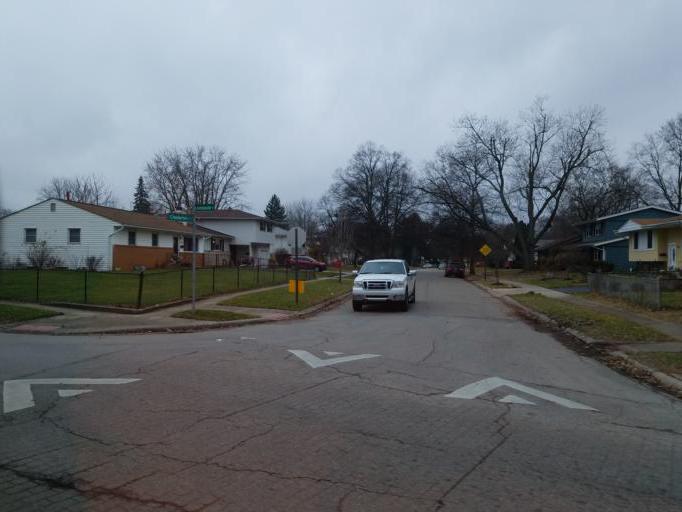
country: US
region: Ohio
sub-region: Franklin County
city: Worthington
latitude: 40.0892
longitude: -82.9808
